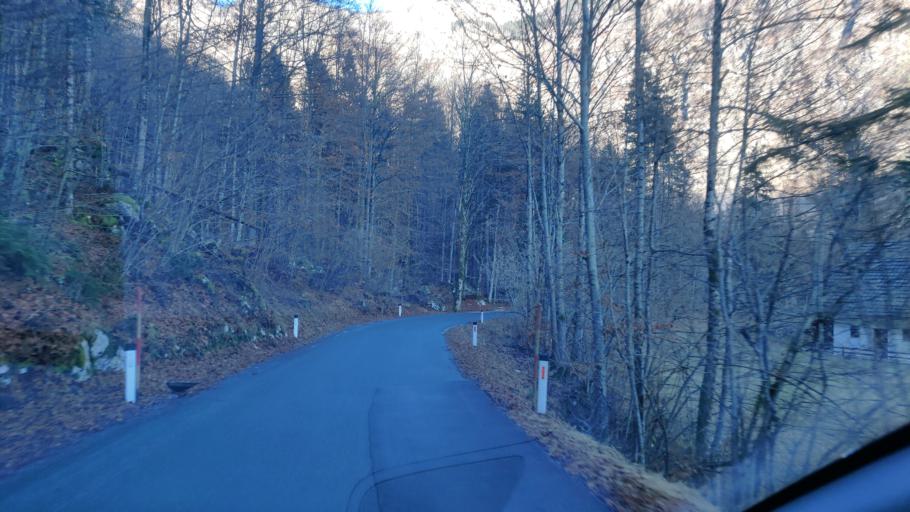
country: SI
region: Tolmin
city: Tolmin
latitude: 46.2795
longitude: 13.8101
